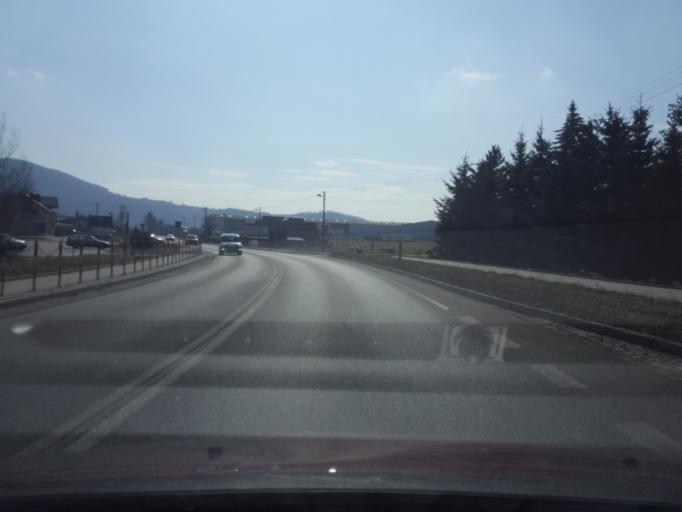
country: PL
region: Lesser Poland Voivodeship
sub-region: Powiat nowosadecki
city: Lososina Dolna
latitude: 49.7087
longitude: 20.6451
